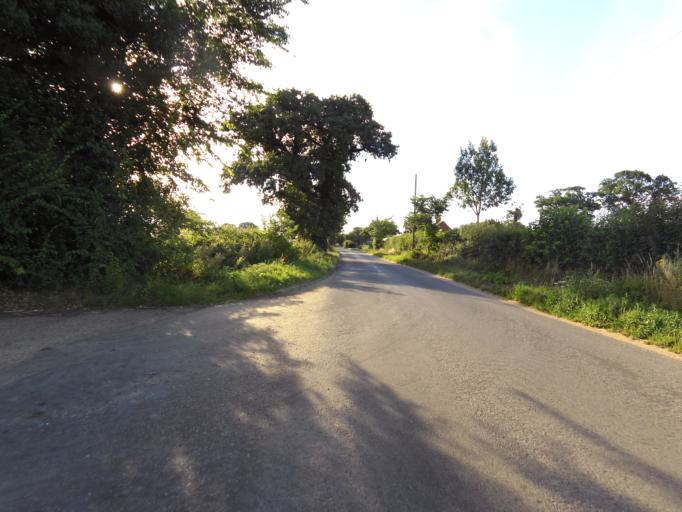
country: GB
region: England
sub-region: Suffolk
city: Kesgrave
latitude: 52.0226
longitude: 1.2123
